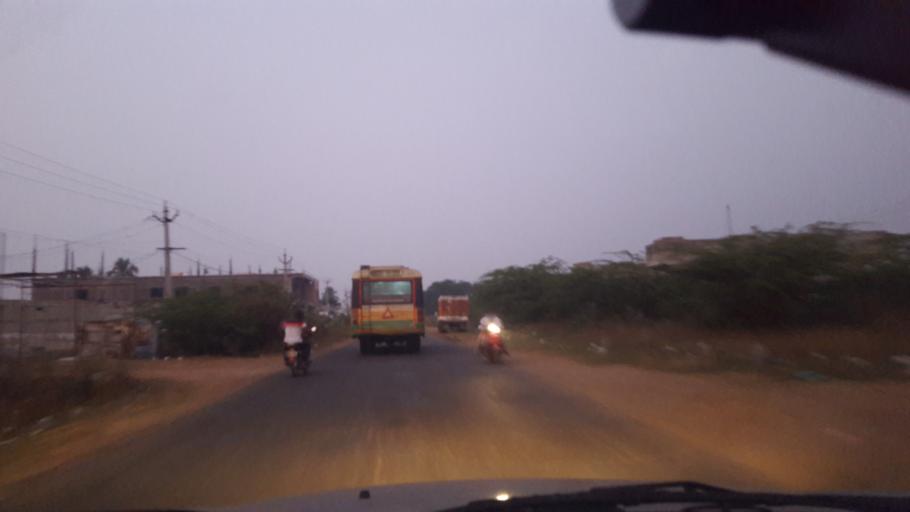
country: IN
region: Andhra Pradesh
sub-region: Srikakulam
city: Palasa
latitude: 18.7528
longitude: 84.4166
